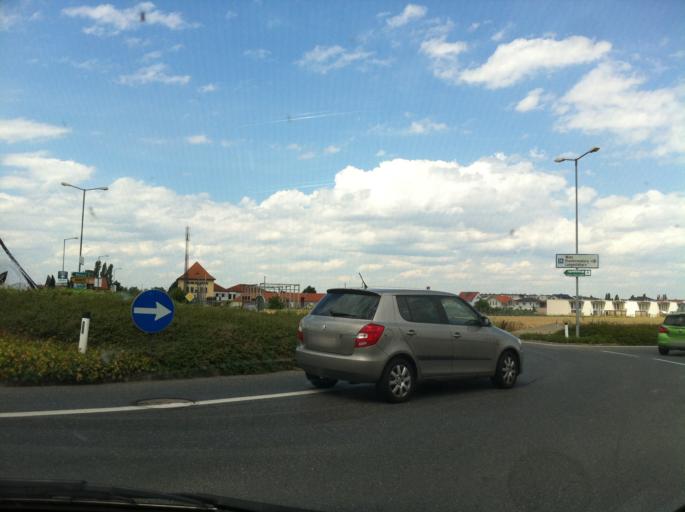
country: AT
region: Lower Austria
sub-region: Politischer Bezirk Tulln
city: Tulln
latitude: 48.3153
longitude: 16.0567
